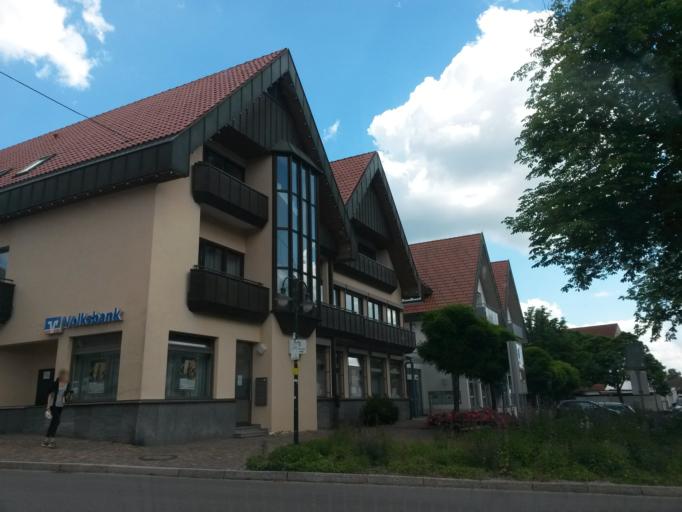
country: DE
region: Baden-Wuerttemberg
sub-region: Karlsruhe Region
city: Pfalzgrafenweiler
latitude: 48.5258
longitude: 8.5648
